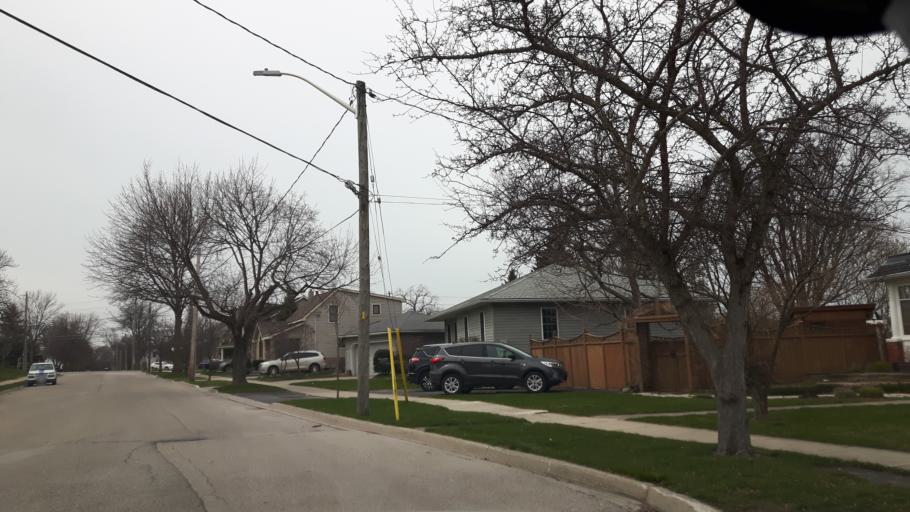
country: CA
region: Ontario
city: Goderich
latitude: 43.7503
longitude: -81.7064
